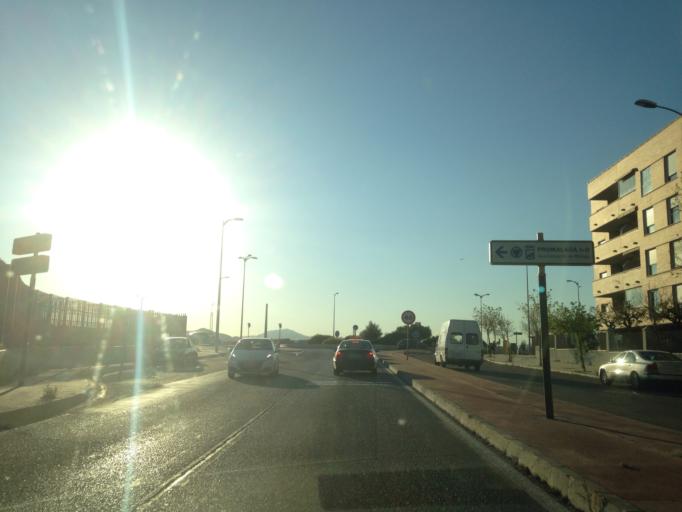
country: ES
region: Andalusia
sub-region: Provincia de Malaga
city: Malaga
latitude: 36.7029
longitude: -4.4916
